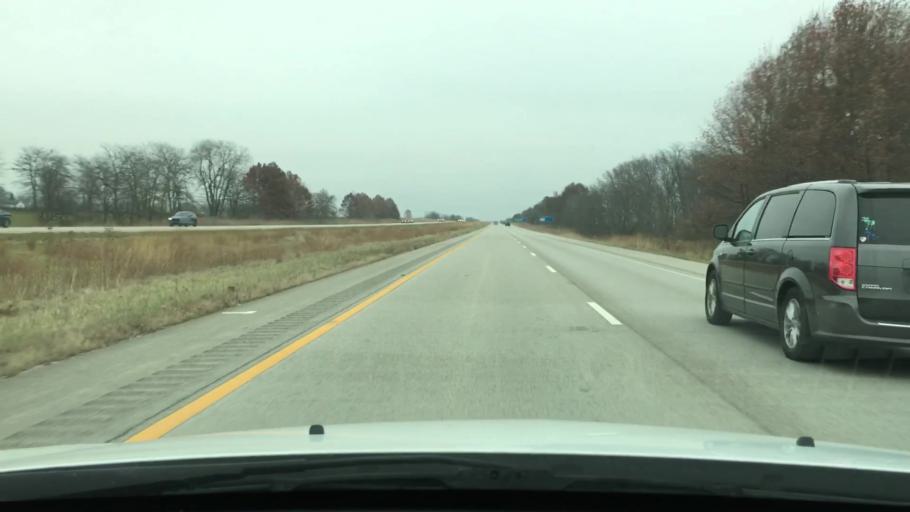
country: US
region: Illinois
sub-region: Sangamon County
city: New Berlin
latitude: 39.7398
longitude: -89.9587
